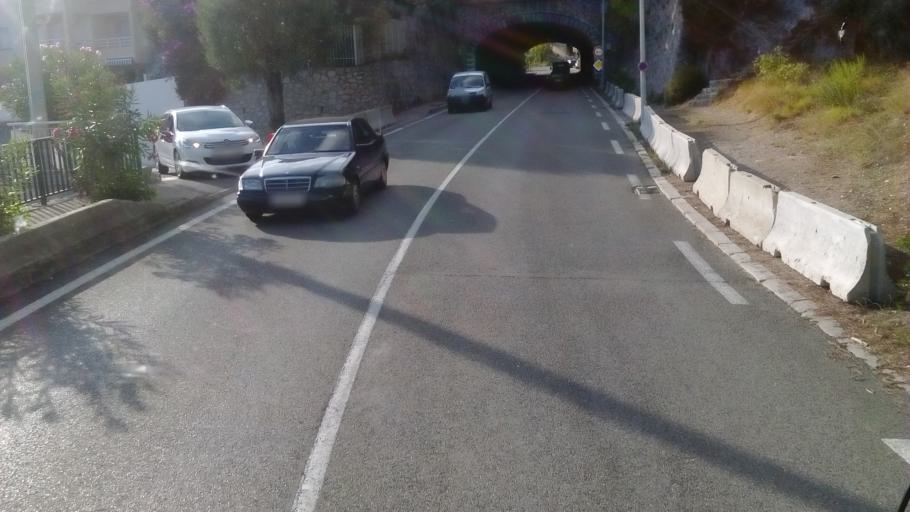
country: MC
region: Commune de Monaco
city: Saint-Roman
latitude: 43.7538
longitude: 7.4376
